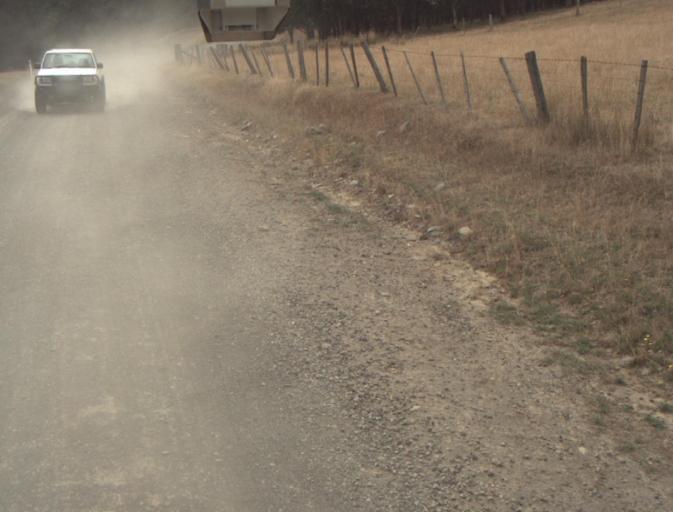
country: AU
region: Tasmania
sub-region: Dorset
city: Scottsdale
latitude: -41.4702
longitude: 147.5905
